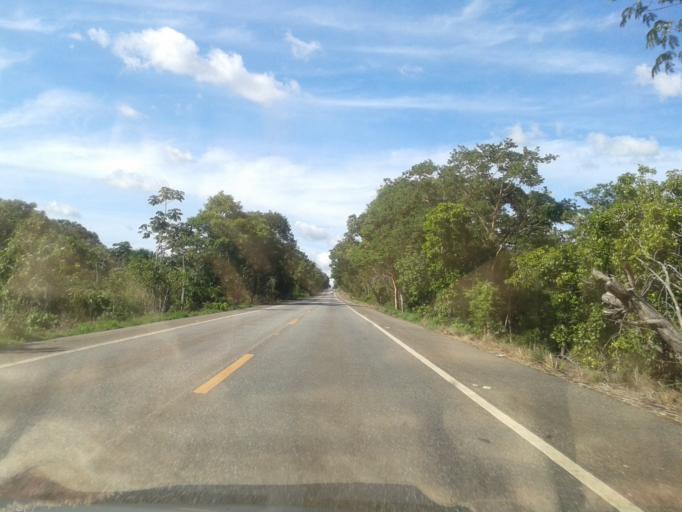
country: BR
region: Goias
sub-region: Mozarlandia
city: Mozarlandia
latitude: -14.9594
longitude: -50.5793
